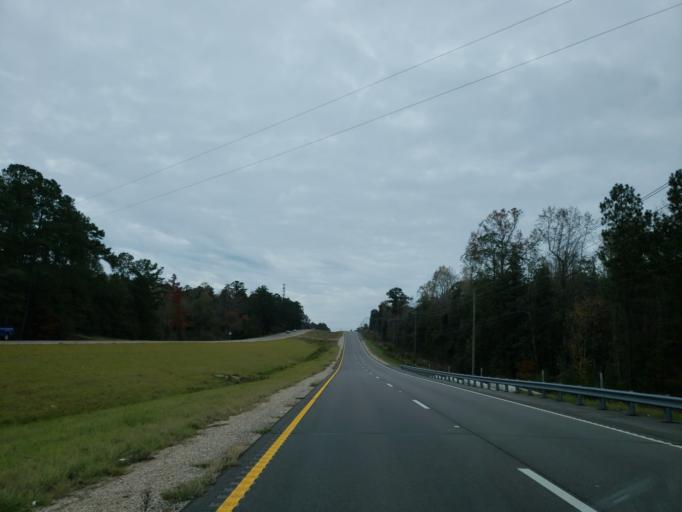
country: US
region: Mississippi
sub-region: Forrest County
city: Hattiesburg
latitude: 31.2287
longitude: -89.2693
